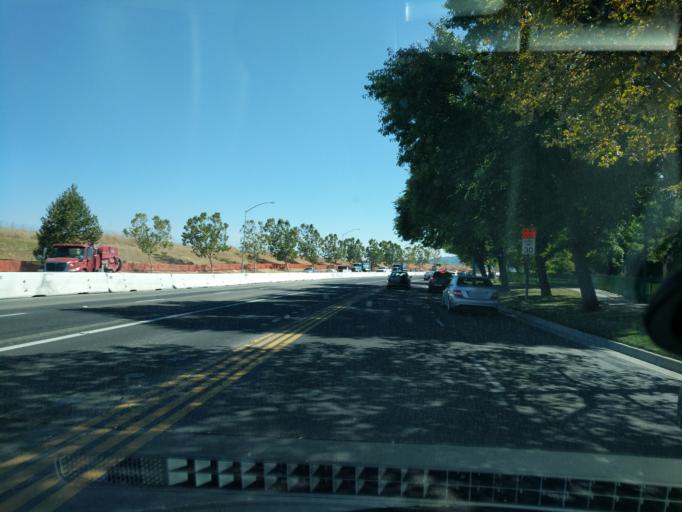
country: US
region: California
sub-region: Alameda County
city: Dublin
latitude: 37.7253
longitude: -121.9096
